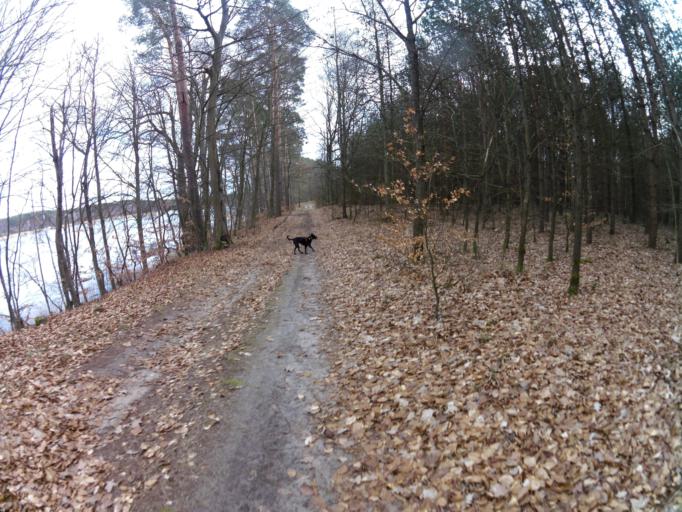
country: PL
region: Lubusz
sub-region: Powiat gorzowski
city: Lubiszyn
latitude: 52.7870
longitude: 14.8407
